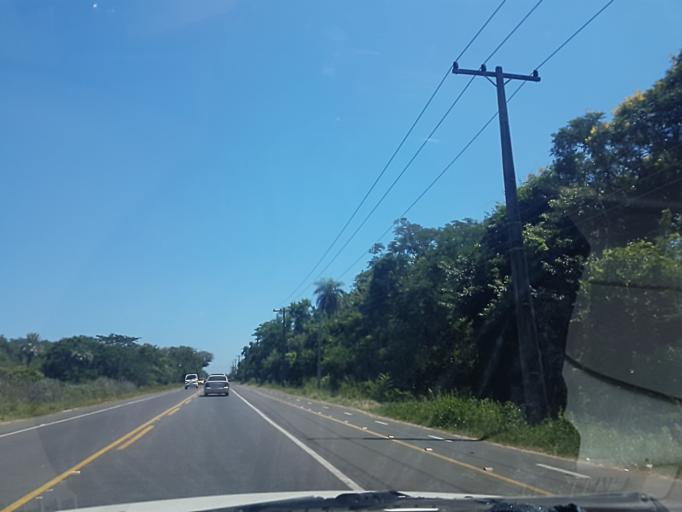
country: PY
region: Central
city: Limpio
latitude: -25.2156
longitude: -57.4167
